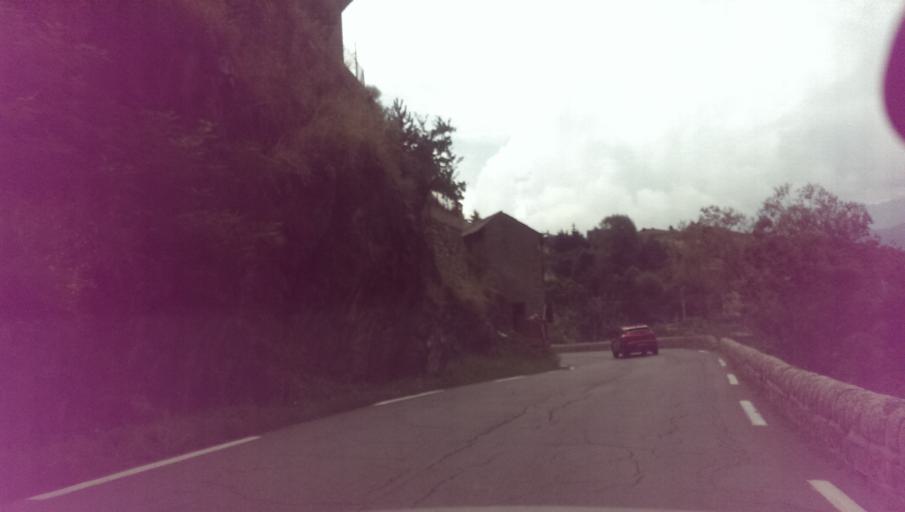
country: ES
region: Catalonia
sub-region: Provincia de Girona
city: Llivia
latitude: 42.5110
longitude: 2.1278
